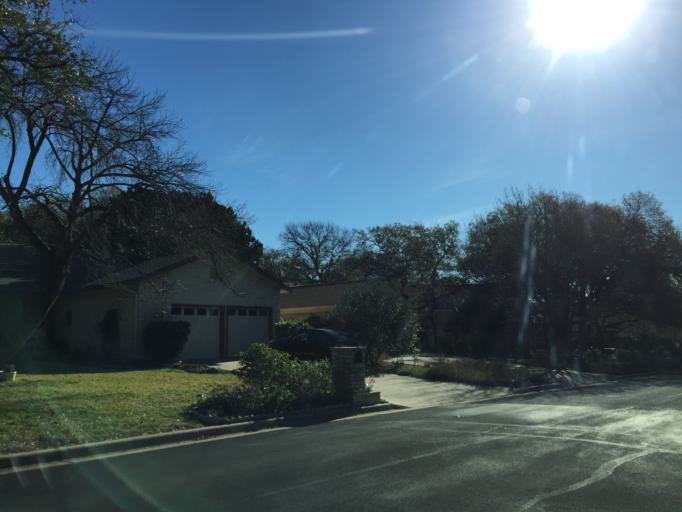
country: US
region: Texas
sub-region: Williamson County
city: Jollyville
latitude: 30.4051
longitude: -97.7321
